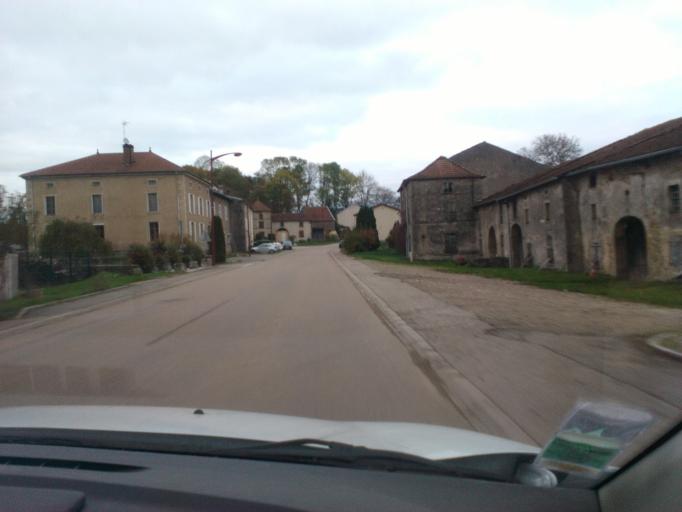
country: FR
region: Lorraine
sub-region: Departement des Vosges
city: Darnieulles
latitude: 48.2430
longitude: 6.3399
